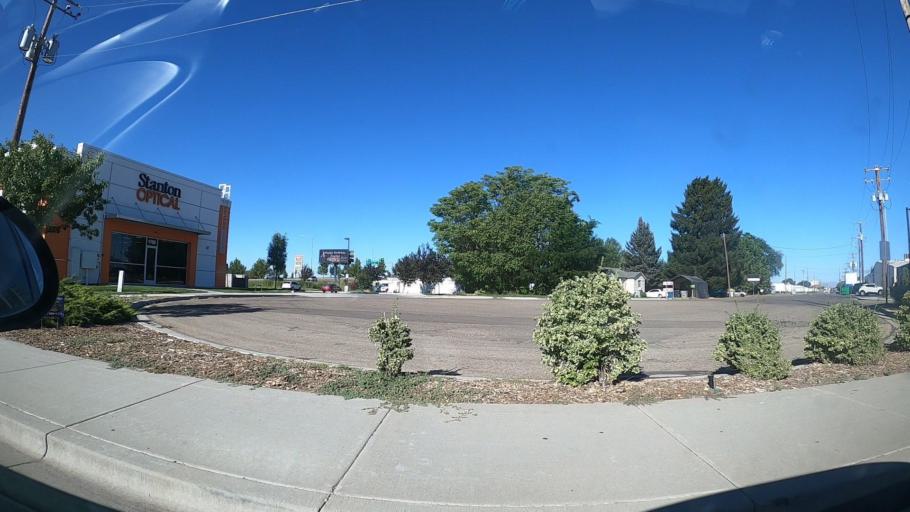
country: US
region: Idaho
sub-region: Canyon County
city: Nampa
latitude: 43.6044
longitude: -116.6013
